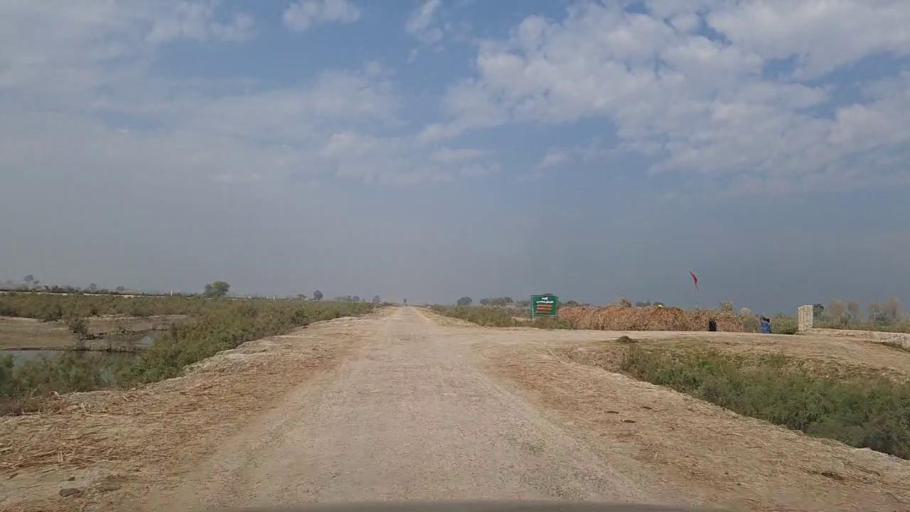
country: PK
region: Sindh
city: Daur
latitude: 26.3912
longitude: 68.3501
